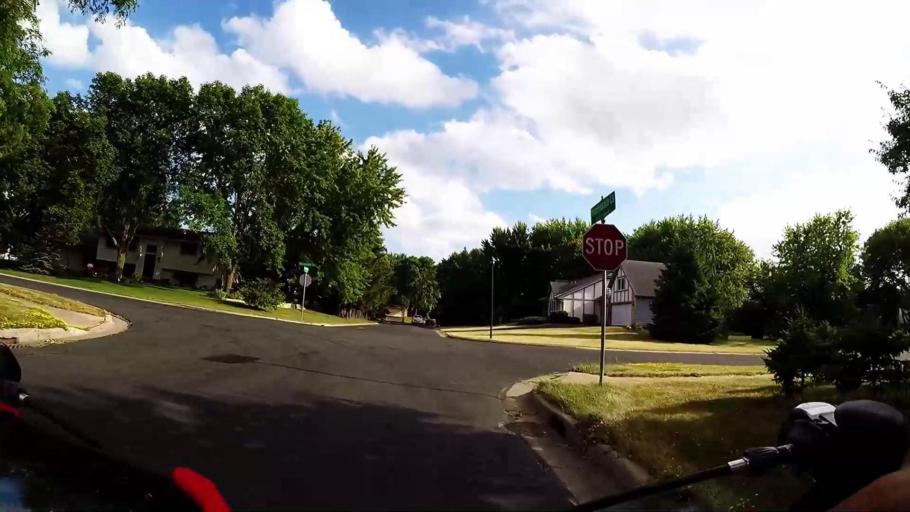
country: US
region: Minnesota
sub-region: Hennepin County
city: Minnetonka
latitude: 44.8827
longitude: -93.4924
